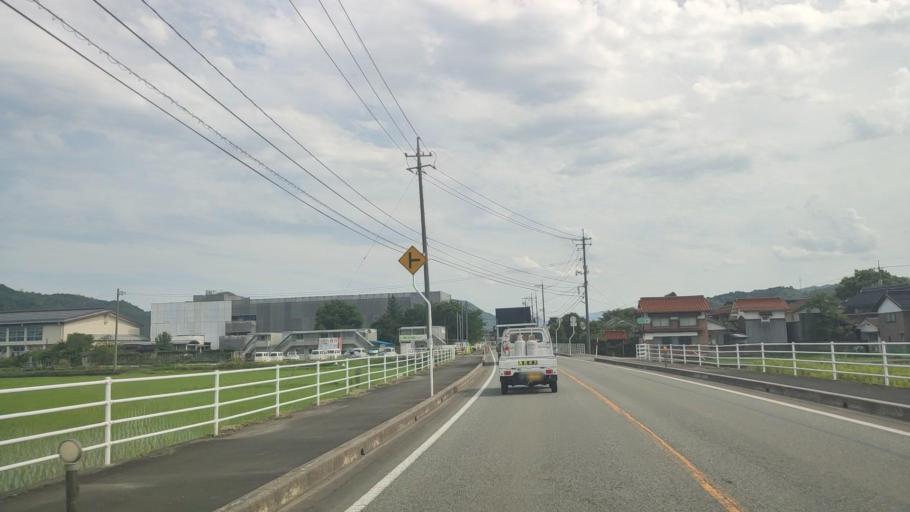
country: JP
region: Tottori
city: Tottori
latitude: 35.4557
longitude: 134.2032
